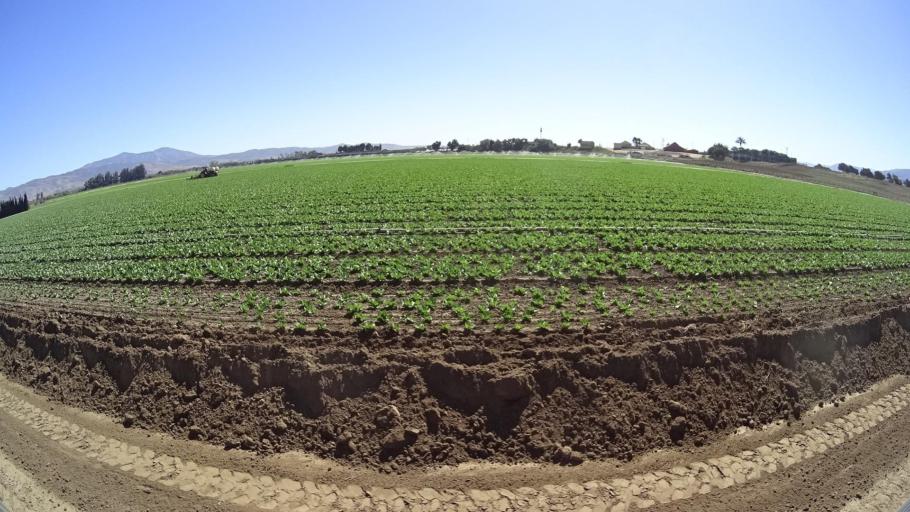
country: US
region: California
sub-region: Monterey County
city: Soledad
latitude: 36.4075
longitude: -121.3492
